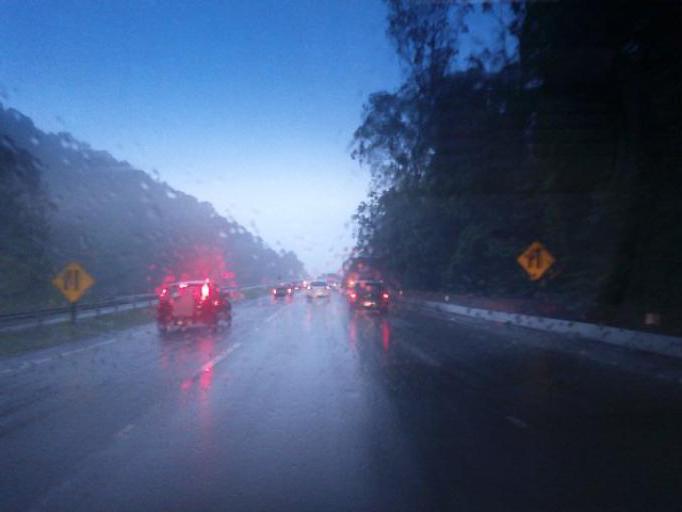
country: BR
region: Sao Paulo
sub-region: Juquitiba
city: Juquitiba
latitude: -24.0334
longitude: -47.1832
